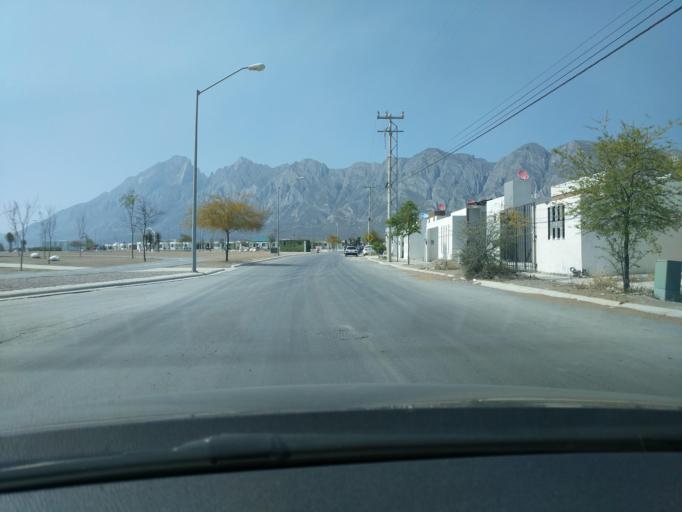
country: MX
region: Nuevo Leon
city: Garcia
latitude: 25.8149
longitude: -100.5391
